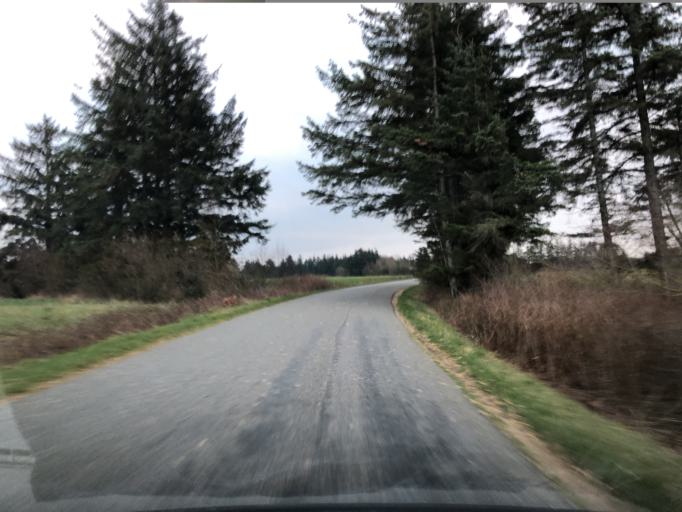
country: DK
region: Central Jutland
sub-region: Holstebro Kommune
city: Ulfborg
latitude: 56.2659
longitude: 8.2849
